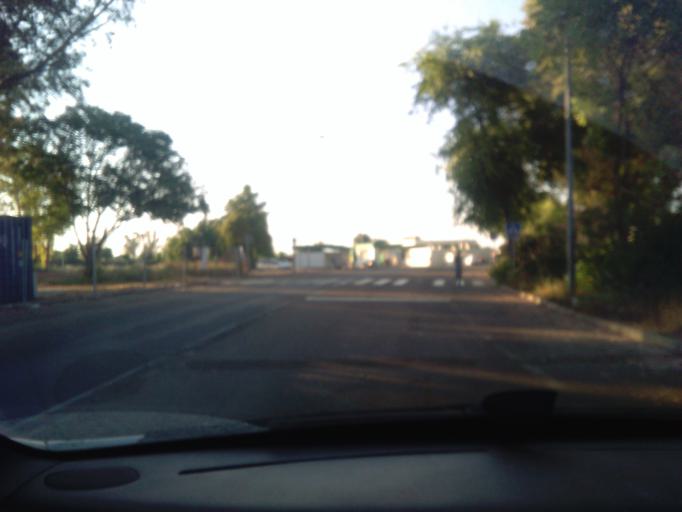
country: ES
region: Andalusia
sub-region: Provincia de Sevilla
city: Sevilla
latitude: 37.4092
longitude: -5.9386
